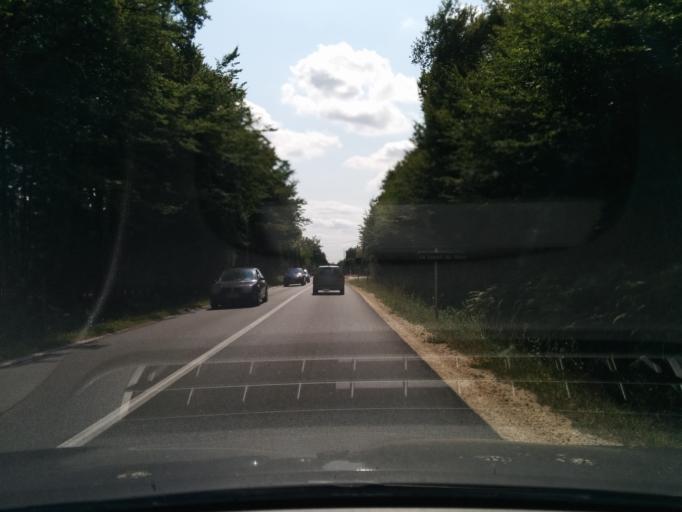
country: FR
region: Centre
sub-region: Departement du Cher
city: Vignoux-sur-Barangeon
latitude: 47.2766
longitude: 2.1772
